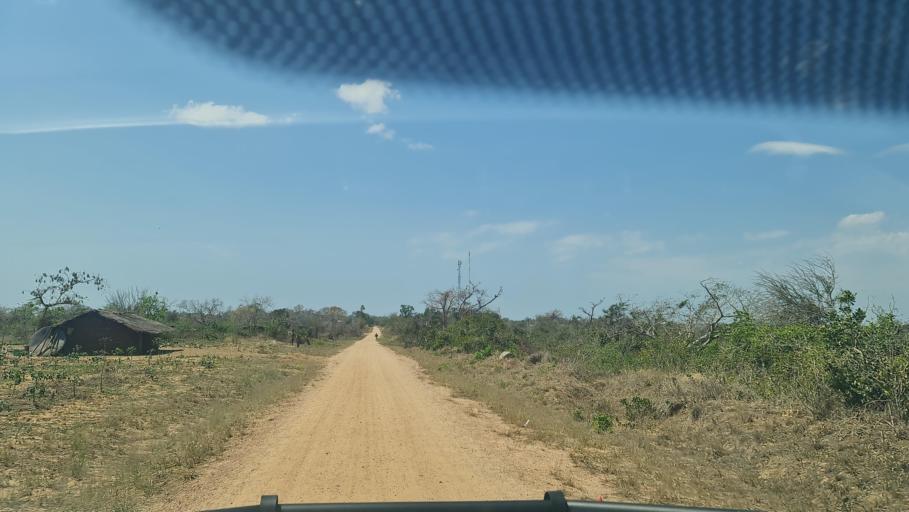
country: MZ
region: Nampula
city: Ilha de Mocambique
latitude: -15.1917
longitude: 40.5220
